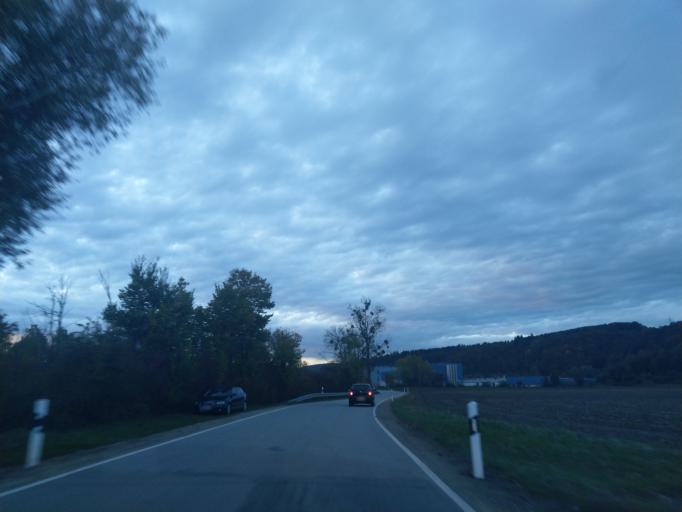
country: DE
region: Bavaria
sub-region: Lower Bavaria
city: Niederalteich
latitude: 48.7864
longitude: 13.0190
